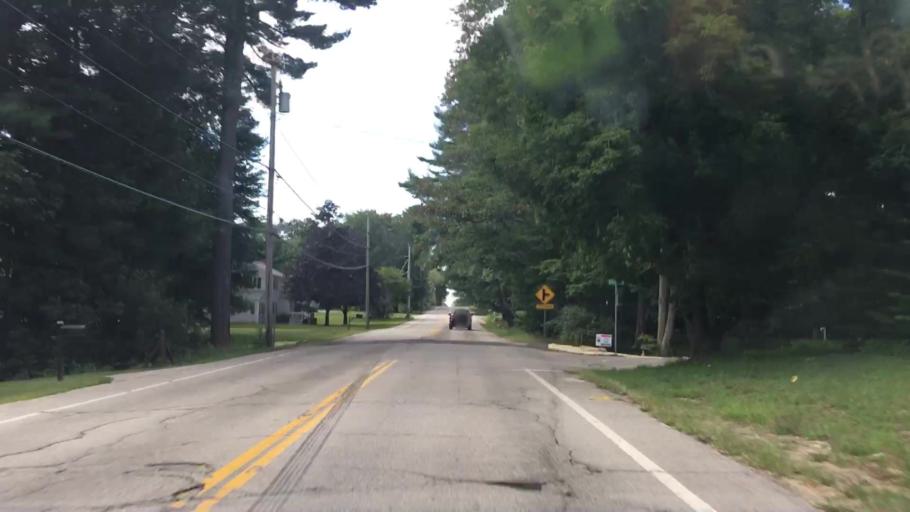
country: US
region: New Hampshire
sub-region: Strafford County
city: Somersworth
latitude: 43.2617
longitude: -70.8936
